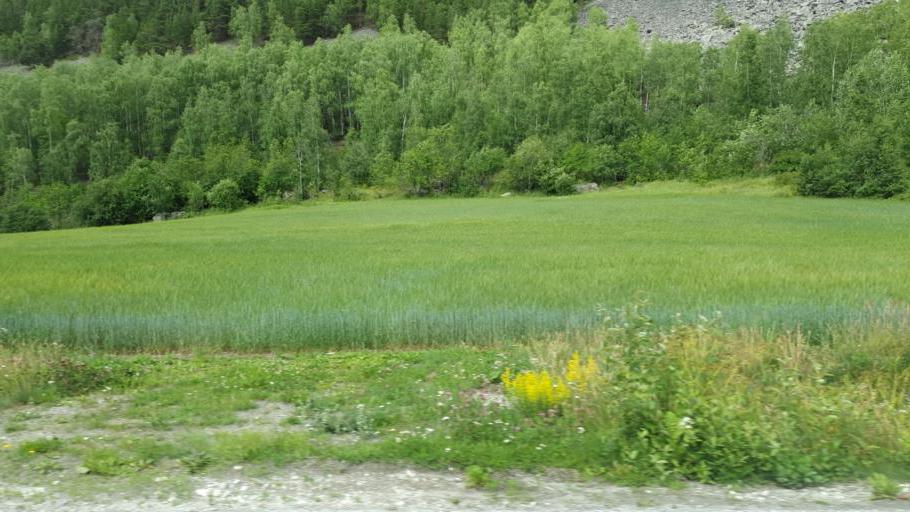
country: NO
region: Oppland
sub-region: Sel
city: Otta
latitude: 61.8422
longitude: 9.3937
